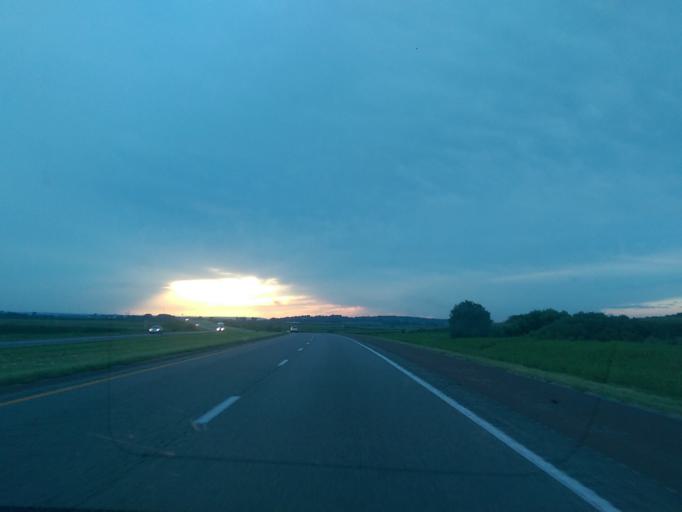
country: US
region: Missouri
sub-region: Holt County
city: Mound City
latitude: 40.1812
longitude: -95.3160
